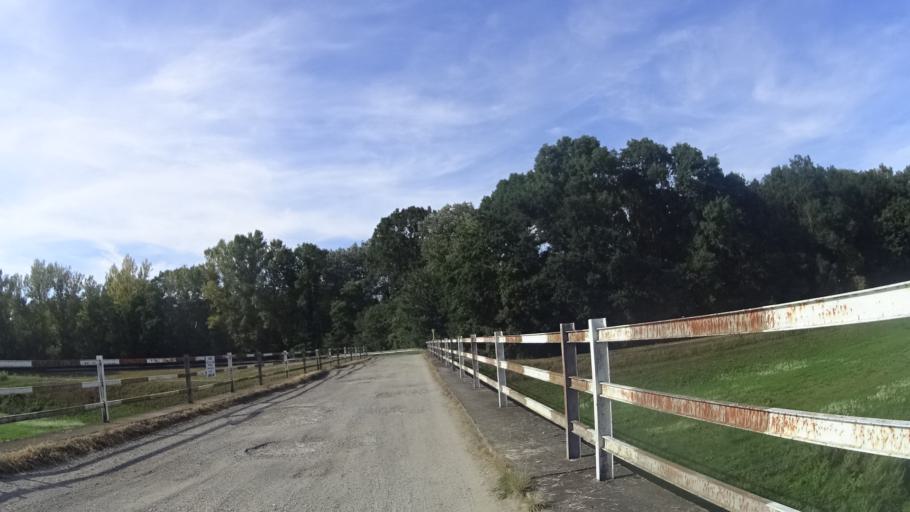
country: AT
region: Lower Austria
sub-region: Politischer Bezirk Ganserndorf
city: Drosing
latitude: 48.4976
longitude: 16.9295
